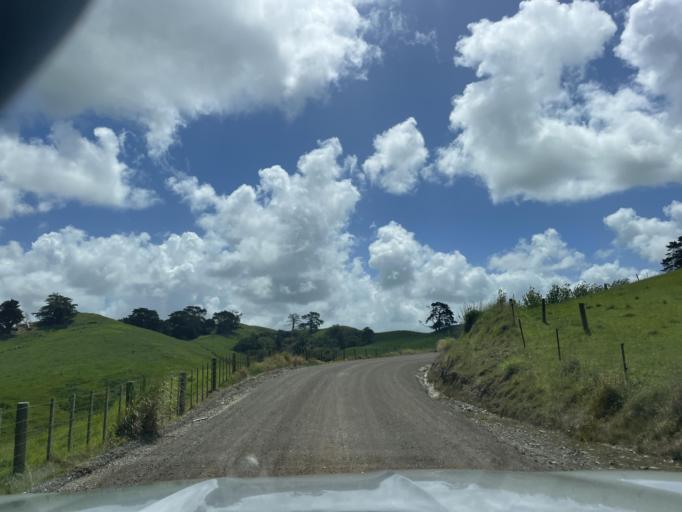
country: NZ
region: Auckland
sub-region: Auckland
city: Wellsford
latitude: -36.1873
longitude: 174.3226
